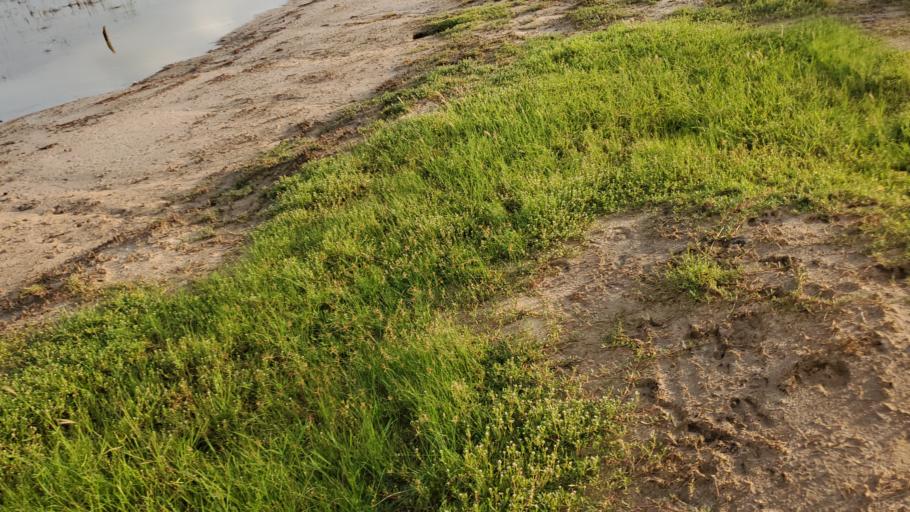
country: SN
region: Saint-Louis
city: Saint-Louis
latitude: 16.0431
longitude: -16.4176
